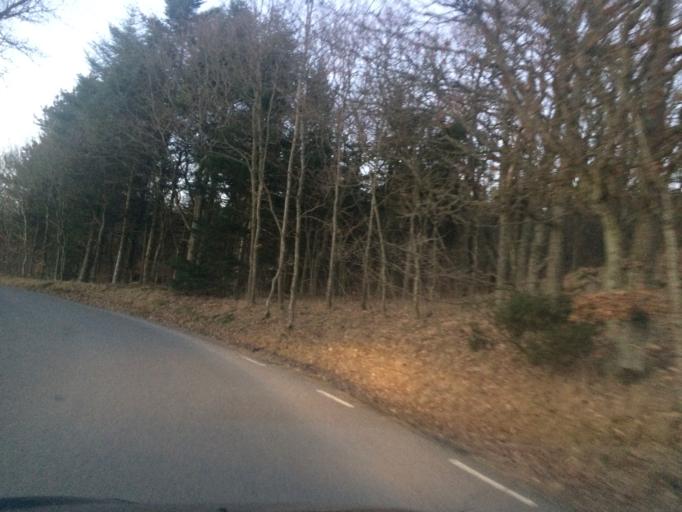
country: SE
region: Vaestra Goetaland
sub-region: Goteborg
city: Torslanda
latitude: 57.7824
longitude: 11.8325
